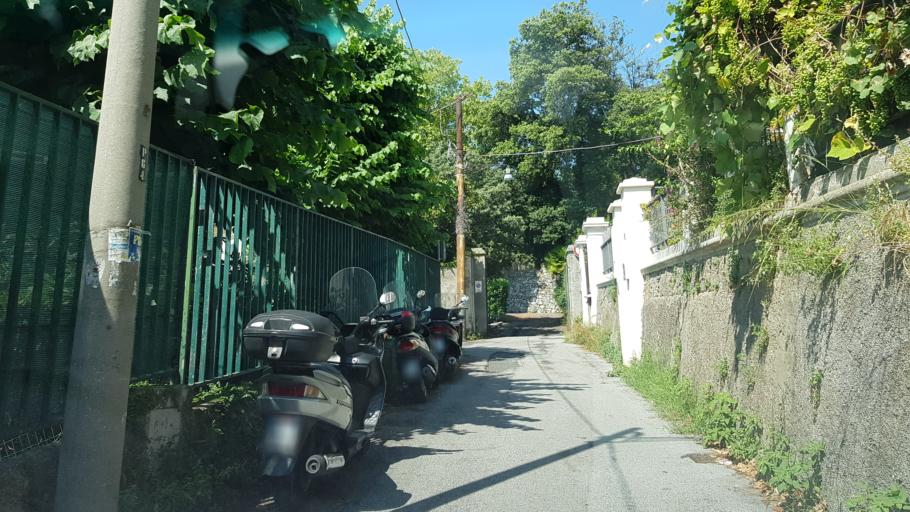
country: IT
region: Liguria
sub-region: Provincia di Genova
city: San Teodoro
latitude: 44.4172
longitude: 8.8659
